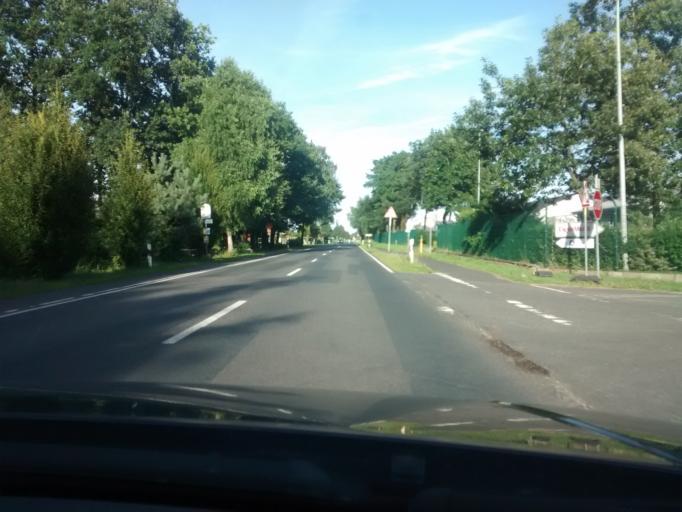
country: DE
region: Lower Saxony
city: Meppen
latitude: 52.6683
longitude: 7.1955
